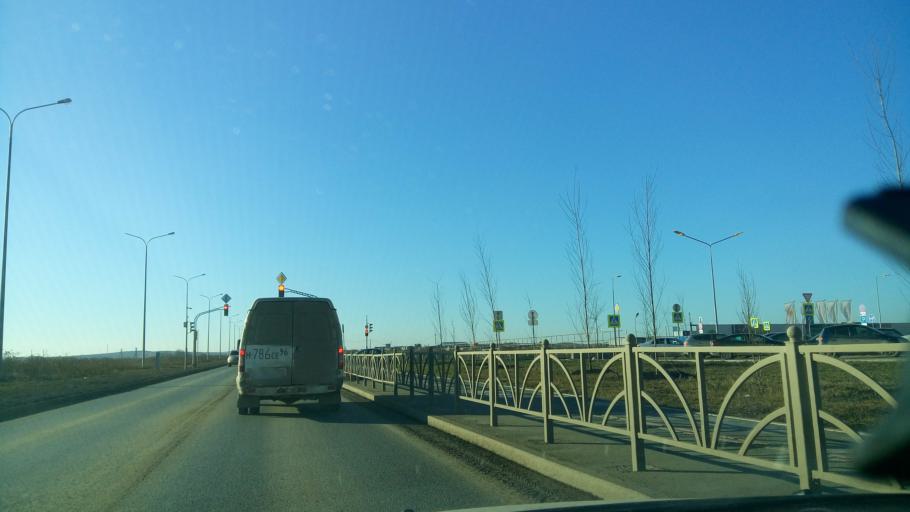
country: RU
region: Sverdlovsk
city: Sovkhoznyy
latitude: 56.7440
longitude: 60.5689
